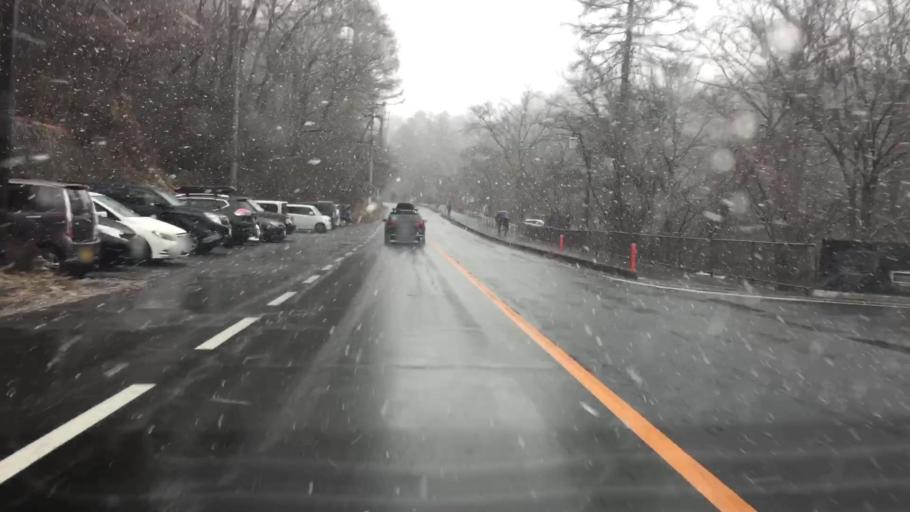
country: JP
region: Nagano
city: Komoro
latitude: 36.3576
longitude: 138.5902
